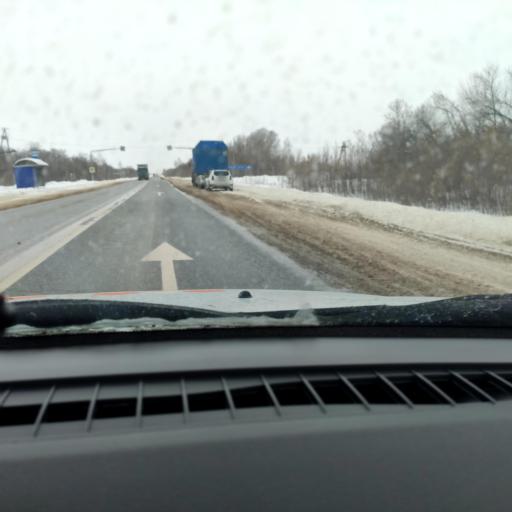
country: RU
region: Samara
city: Dubovyy Umet
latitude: 52.8754
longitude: 50.4352
